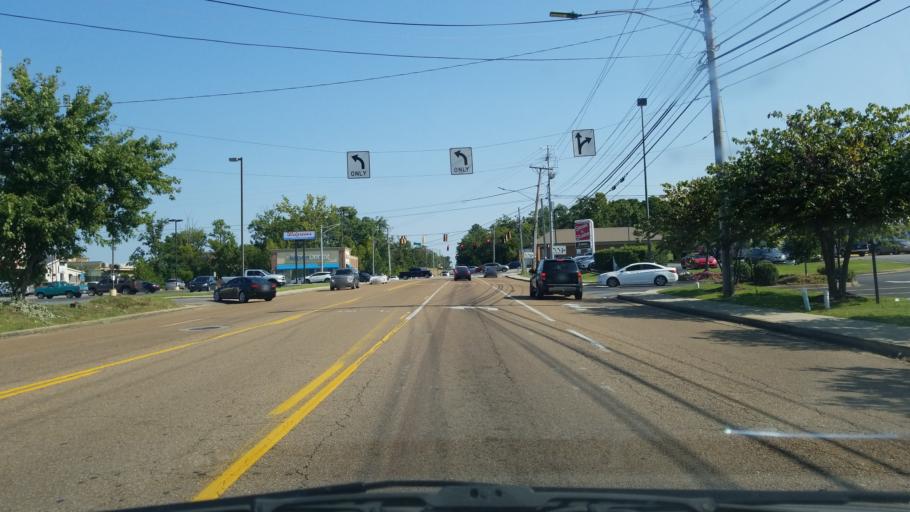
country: US
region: Tennessee
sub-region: Hamilton County
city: East Brainerd
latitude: 35.0393
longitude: -85.1505
